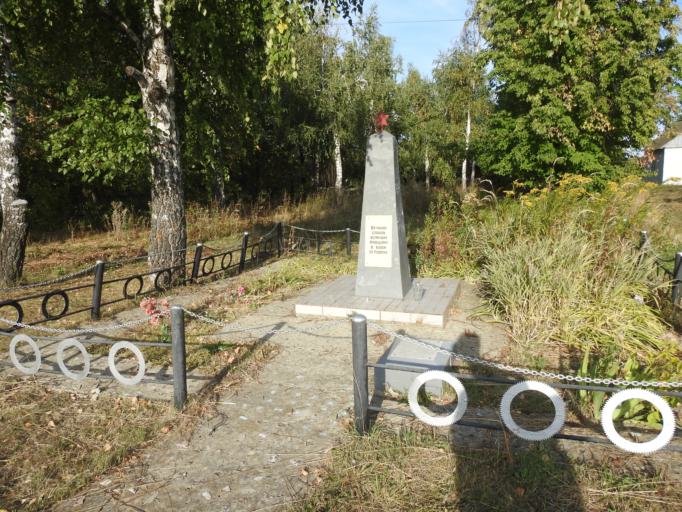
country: RU
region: Saratov
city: Novyye Burasy
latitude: 52.2098
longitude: 46.1231
